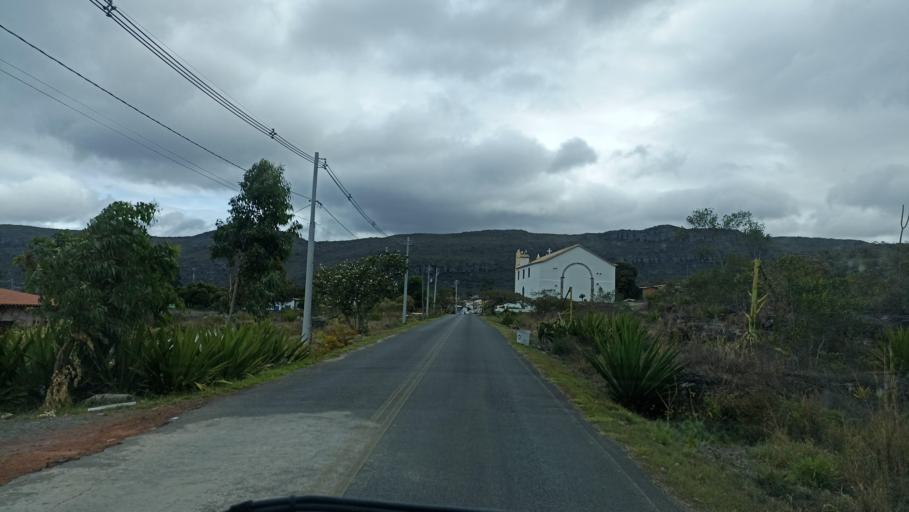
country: BR
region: Bahia
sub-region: Andarai
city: Vera Cruz
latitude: -13.0026
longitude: -41.3663
